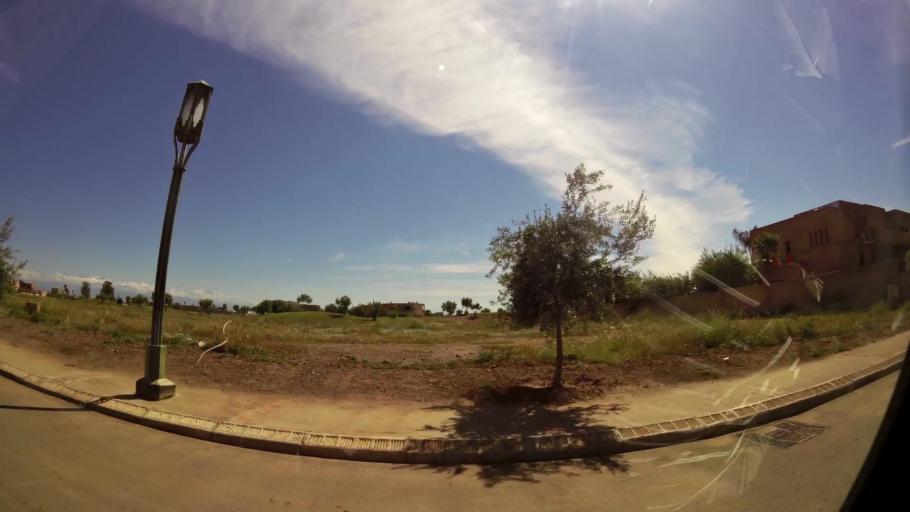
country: MA
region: Marrakech-Tensift-Al Haouz
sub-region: Marrakech
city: Marrakesh
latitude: 31.6211
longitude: -7.9230
